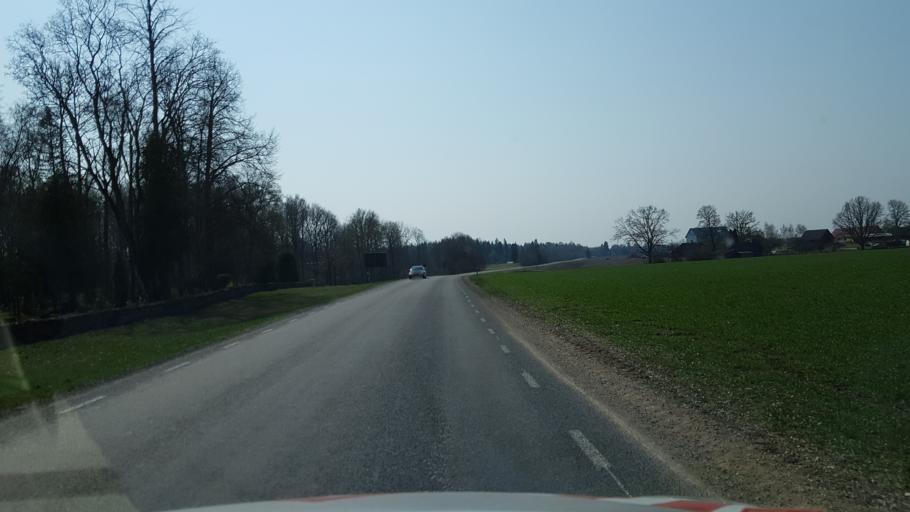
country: EE
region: Raplamaa
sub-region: Kehtna vald
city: Kehtna
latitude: 59.0534
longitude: 24.9502
